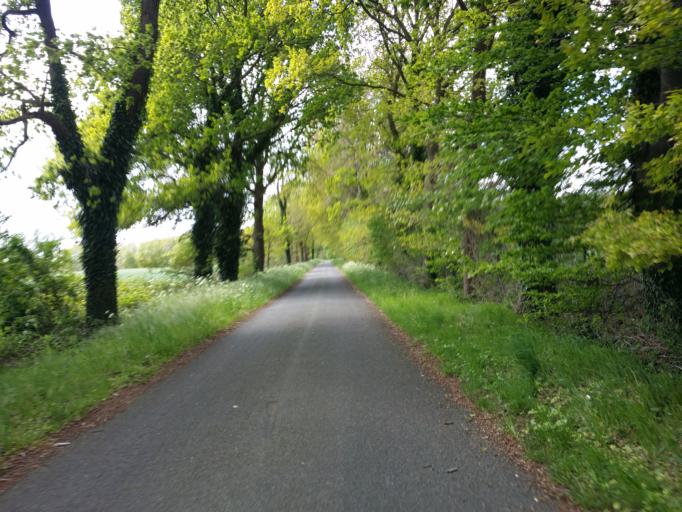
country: DE
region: Lower Saxony
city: Gross Ippener
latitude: 52.9829
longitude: 8.6090
